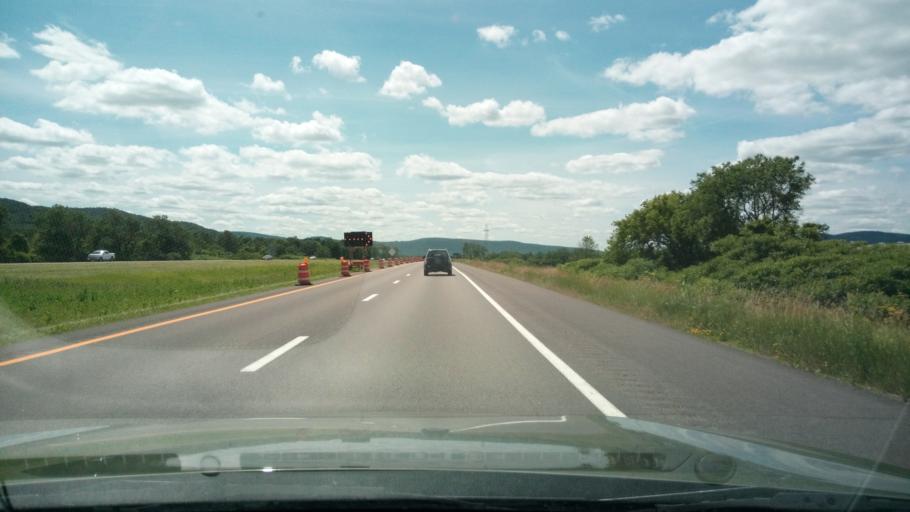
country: US
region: Pennsylvania
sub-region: Bradford County
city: South Waverly
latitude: 42.0012
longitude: -76.5725
